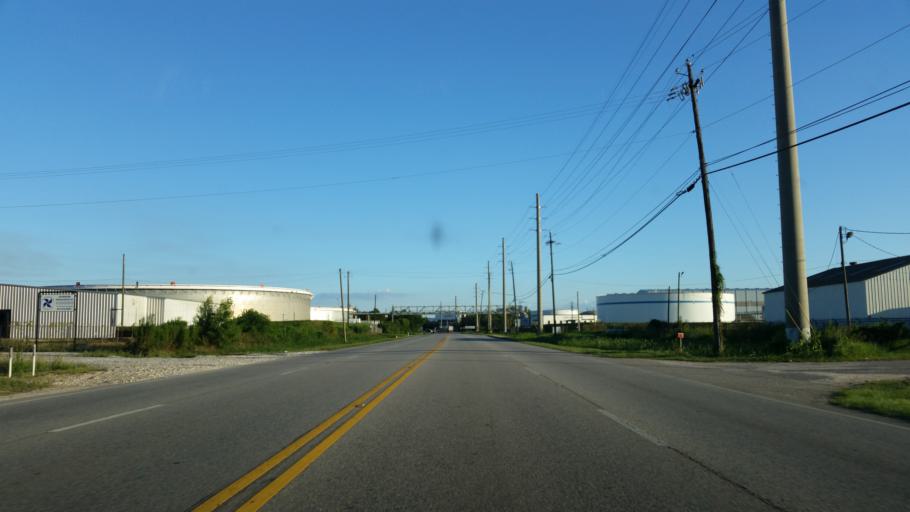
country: US
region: Alabama
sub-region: Mobile County
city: Mobile
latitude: 30.6996
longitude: -88.0324
